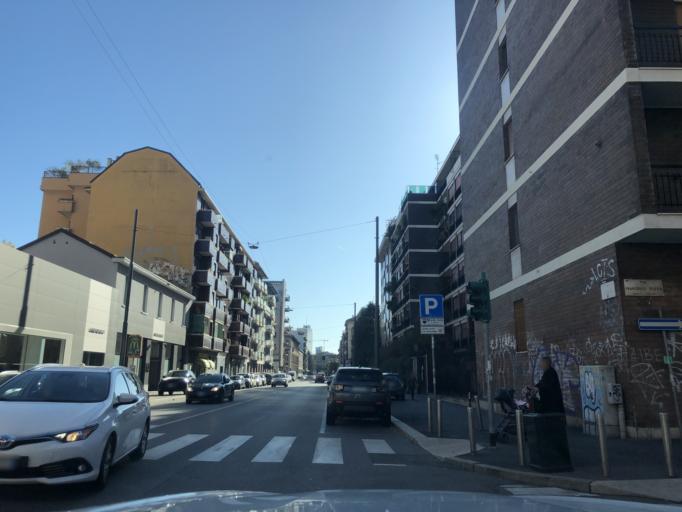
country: IT
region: Lombardy
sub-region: Citta metropolitana di Milano
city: Milano
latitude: 45.4947
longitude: 9.1914
